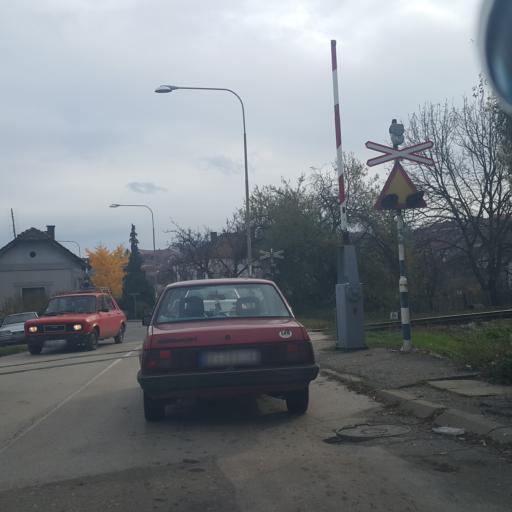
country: RS
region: Central Serbia
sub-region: Zajecarski Okrug
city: Knjazevac
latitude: 43.5689
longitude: 22.2488
